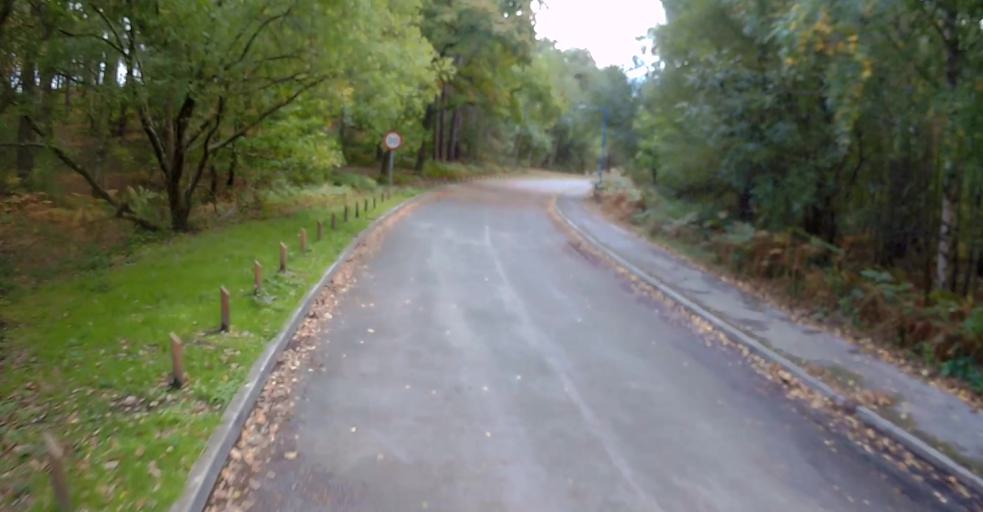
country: GB
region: England
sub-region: Surrey
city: Frimley
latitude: 51.3089
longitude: -0.6992
